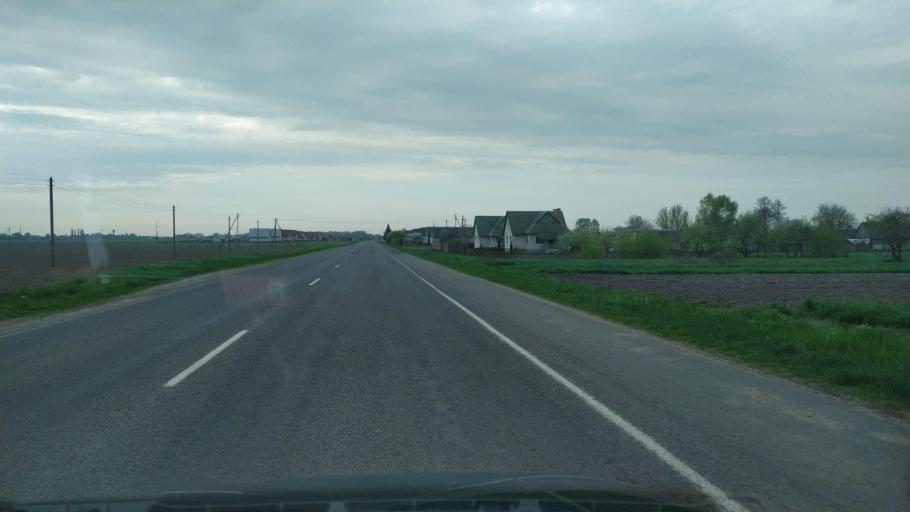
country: BY
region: Brest
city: Kamyanyets
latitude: 52.3320
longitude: 23.9135
